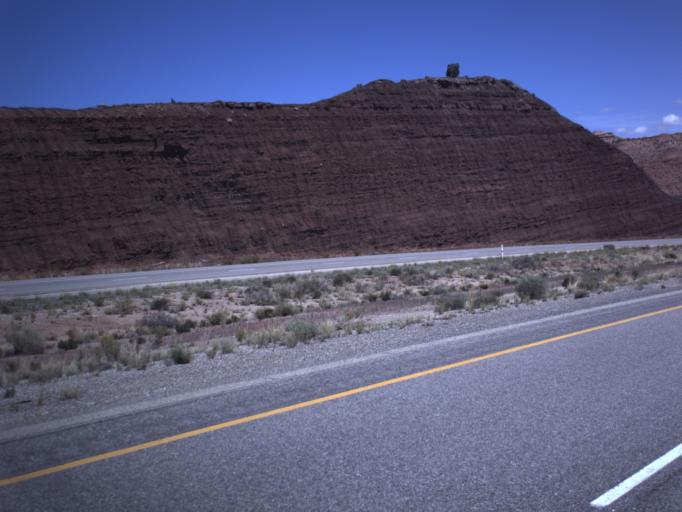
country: US
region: Utah
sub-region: Emery County
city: Ferron
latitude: 38.8314
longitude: -111.1336
